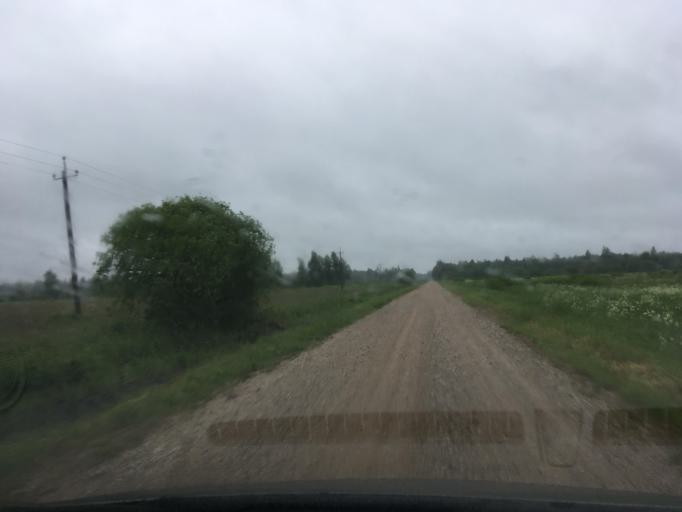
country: EE
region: Laeaene
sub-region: Lihula vald
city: Lihula
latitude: 58.6052
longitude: 23.8315
